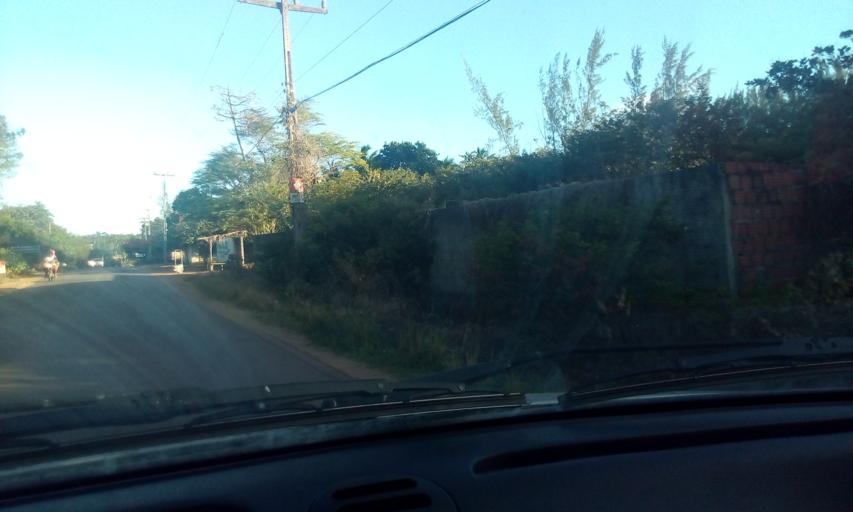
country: BR
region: Rio Grande do Norte
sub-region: Parnamirim
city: Parnamirim
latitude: -5.9561
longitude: -35.1703
